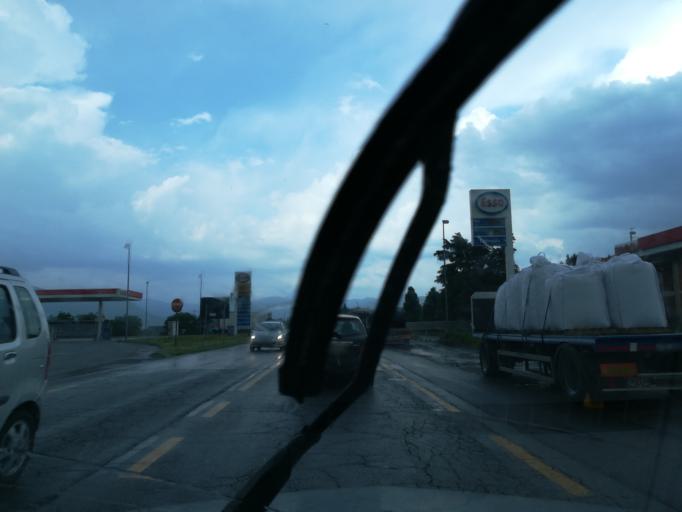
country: IT
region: Lombardy
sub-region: Provincia di Bergamo
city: Curno
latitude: 45.6854
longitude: 9.6024
